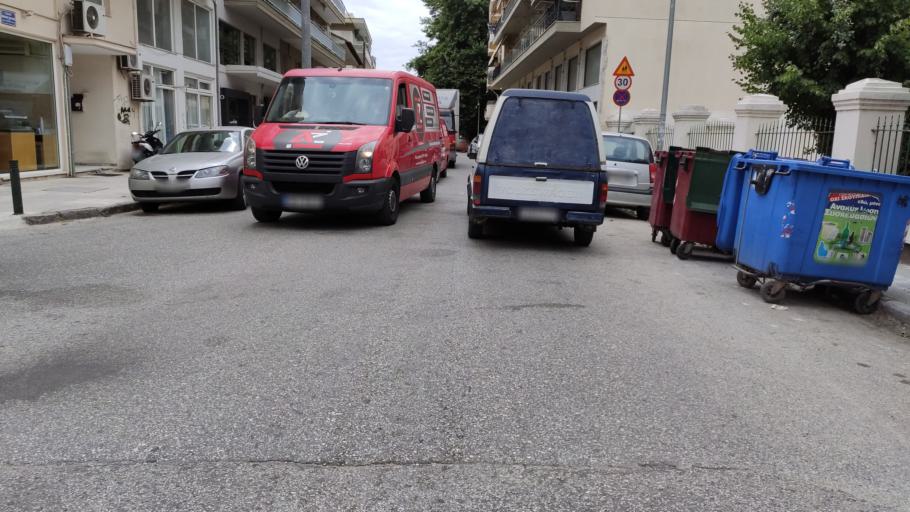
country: GR
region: East Macedonia and Thrace
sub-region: Nomos Rodopis
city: Komotini
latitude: 41.1187
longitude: 25.3940
